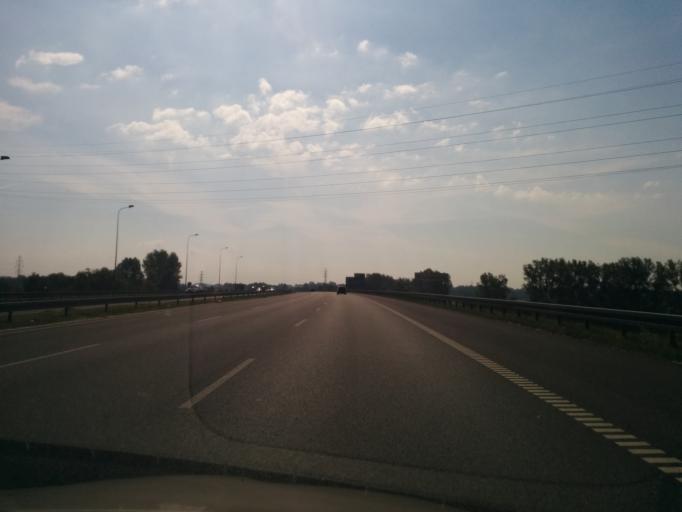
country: PL
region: Silesian Voivodeship
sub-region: Piekary Slaskie
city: Piekary Slaskie
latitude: 50.3704
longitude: 18.9088
